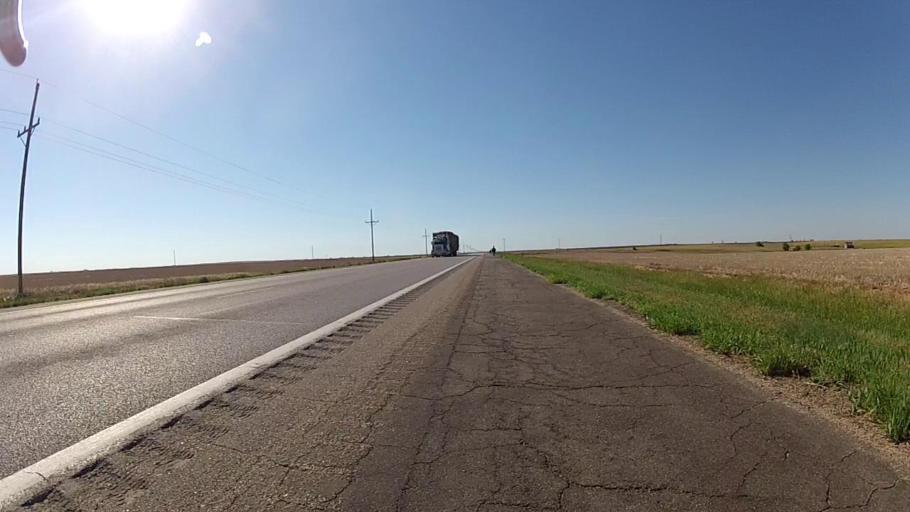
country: US
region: Kansas
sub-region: Ford County
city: Dodge City
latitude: 37.6080
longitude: -99.7105
